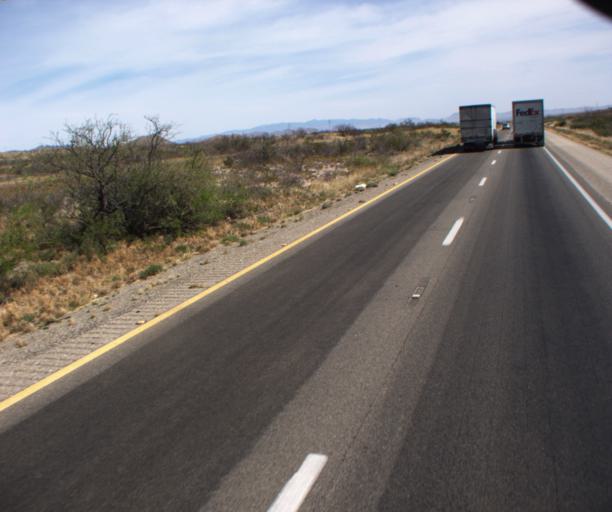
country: US
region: Arizona
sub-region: Cochise County
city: Willcox
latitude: 32.1243
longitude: -110.0135
